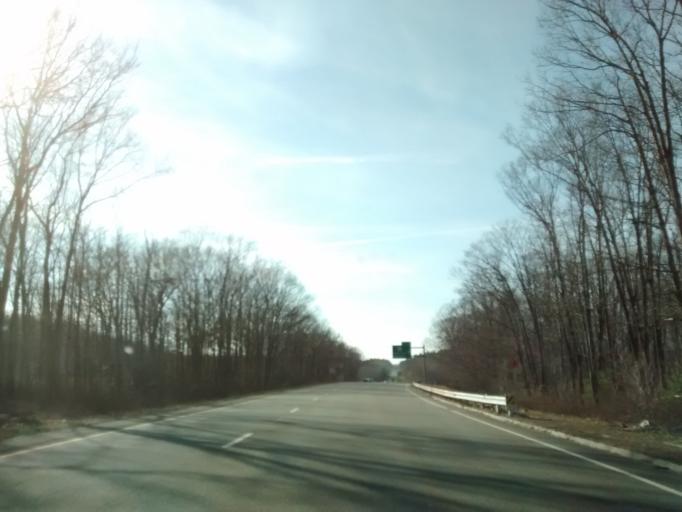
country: US
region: Massachusetts
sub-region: Worcester County
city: Uxbridge
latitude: 42.0644
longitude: -71.6600
